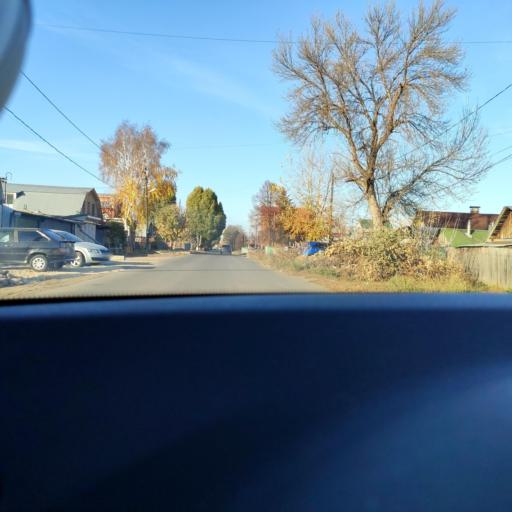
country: RU
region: Samara
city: Petra-Dubrava
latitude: 53.2500
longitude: 50.3284
